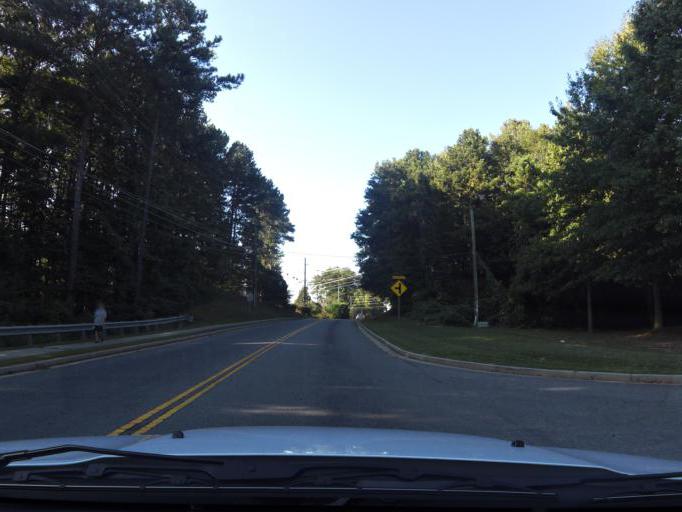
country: US
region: Georgia
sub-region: Cobb County
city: Kennesaw
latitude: 34.0340
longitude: -84.6164
